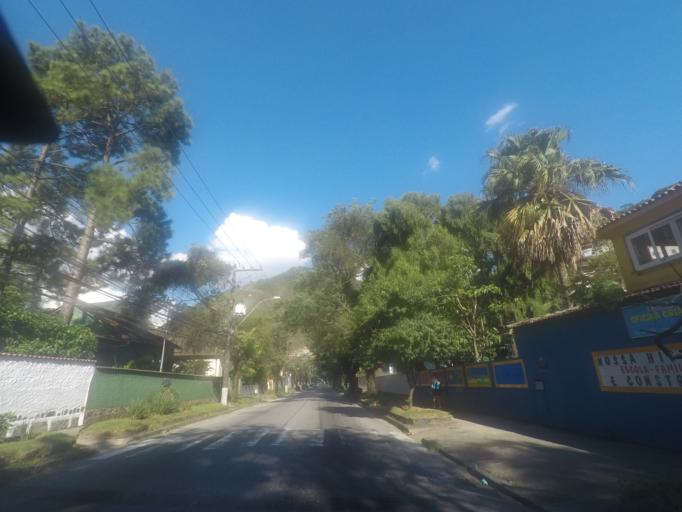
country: BR
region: Rio de Janeiro
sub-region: Petropolis
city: Petropolis
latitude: -22.5278
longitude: -43.1763
